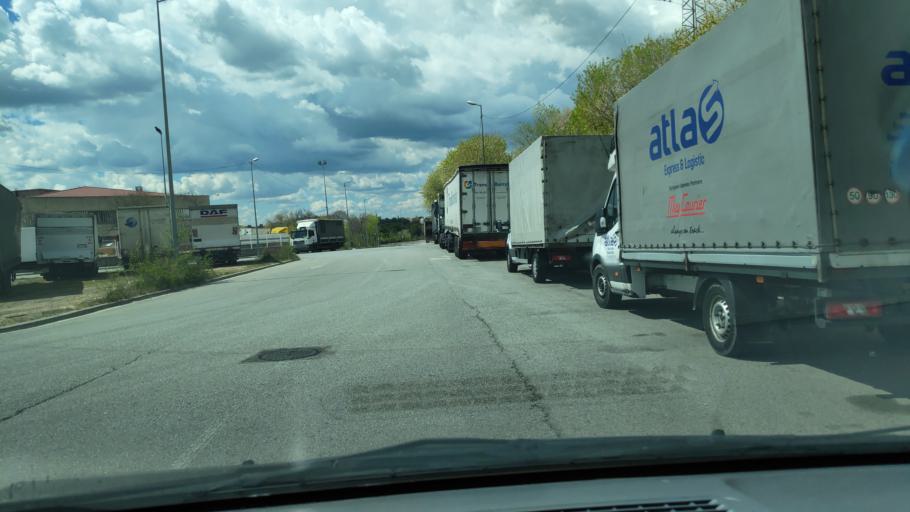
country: ES
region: Catalonia
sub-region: Provincia de Barcelona
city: Polinya
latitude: 41.5445
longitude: 2.1321
